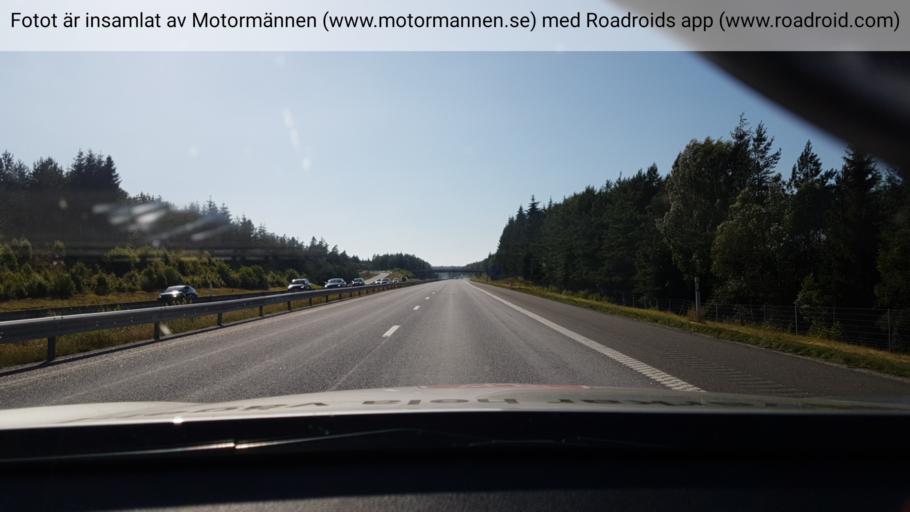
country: SE
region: Vaestra Goetaland
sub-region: Harryda Kommun
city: Hindas
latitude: 57.6730
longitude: 12.3618
